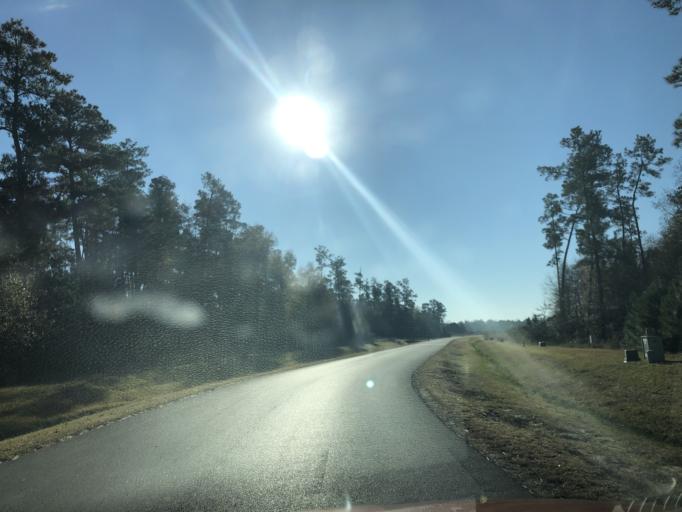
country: US
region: Texas
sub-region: Montgomery County
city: Porter Heights
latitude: 30.0798
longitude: -95.3214
